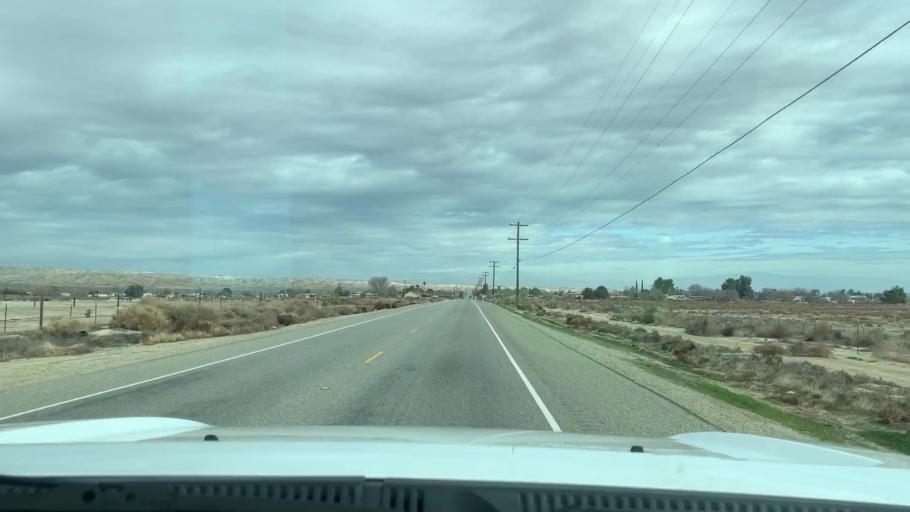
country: US
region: California
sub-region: Kern County
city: Ford City
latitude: 35.2143
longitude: -119.3981
